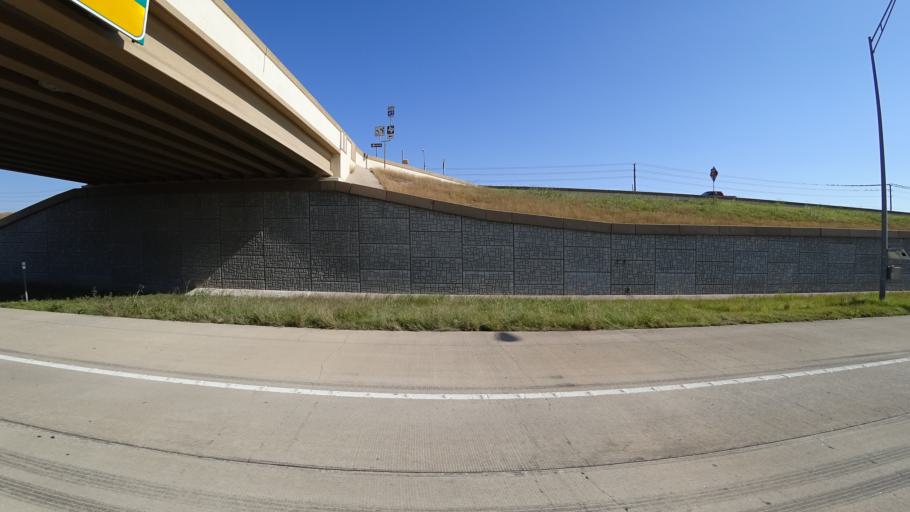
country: US
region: Texas
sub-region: Travis County
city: Pflugerville
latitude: 30.4646
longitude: -97.5941
